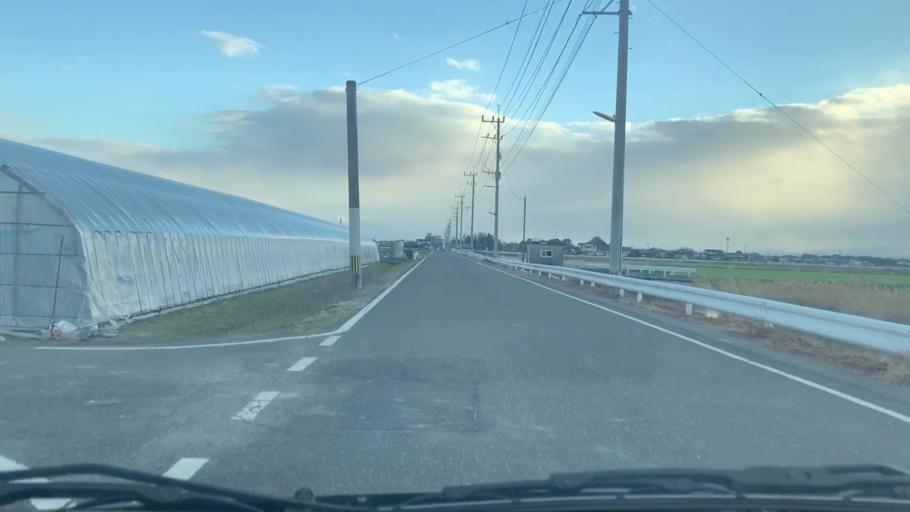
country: JP
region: Saga Prefecture
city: Saga-shi
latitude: 33.2536
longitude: 130.2578
